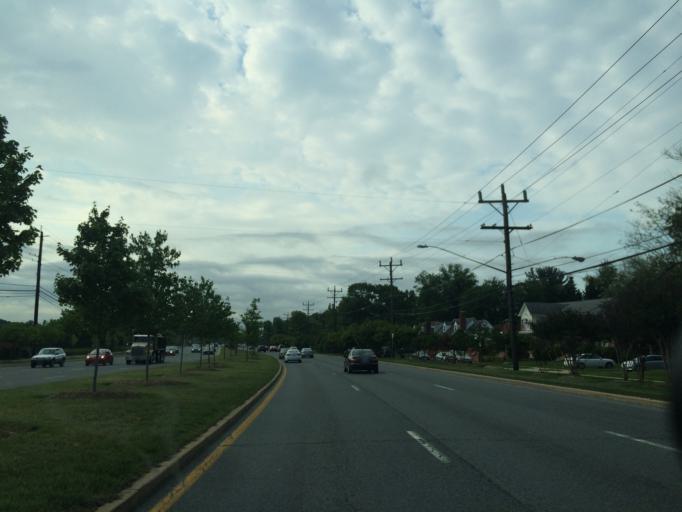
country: US
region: Maryland
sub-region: Montgomery County
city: White Oak
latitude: 39.0360
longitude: -76.9888
